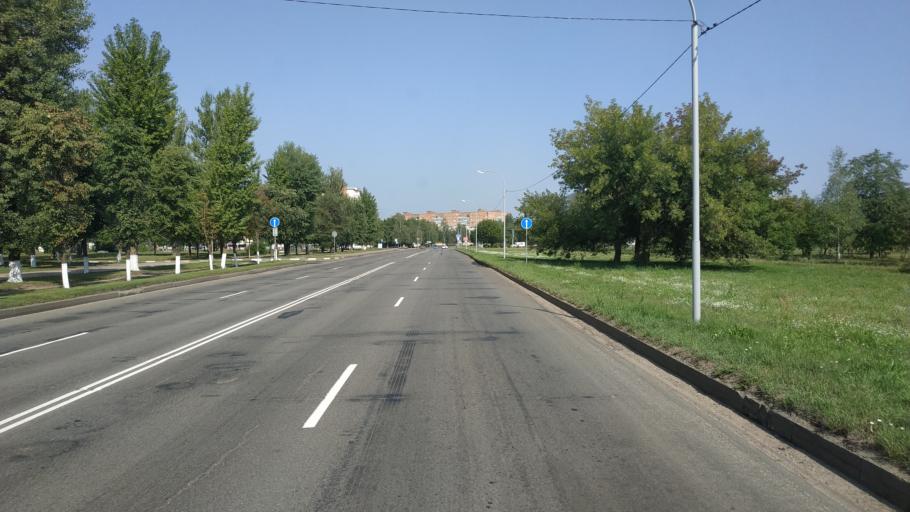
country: BY
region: Mogilev
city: Buynichy
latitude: 53.8646
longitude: 30.3183
